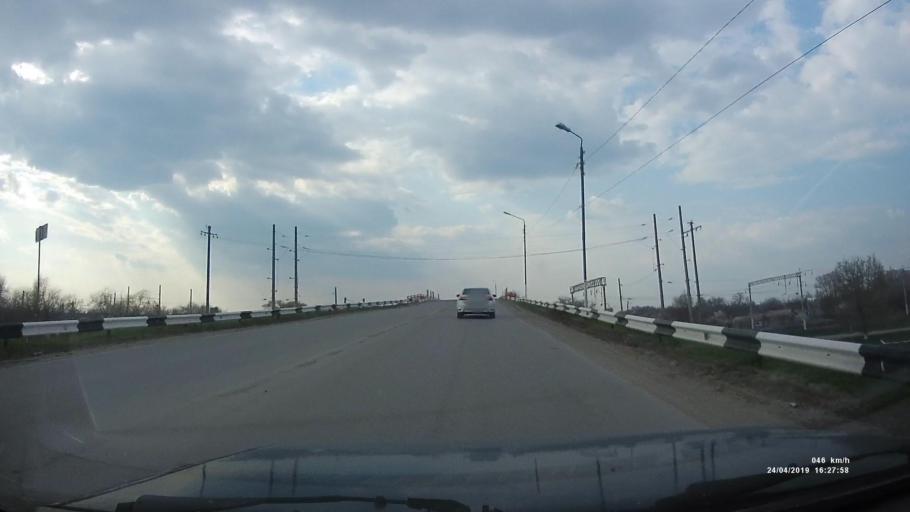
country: RU
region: Rostov
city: Orlovskiy
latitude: 46.8634
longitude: 42.0371
